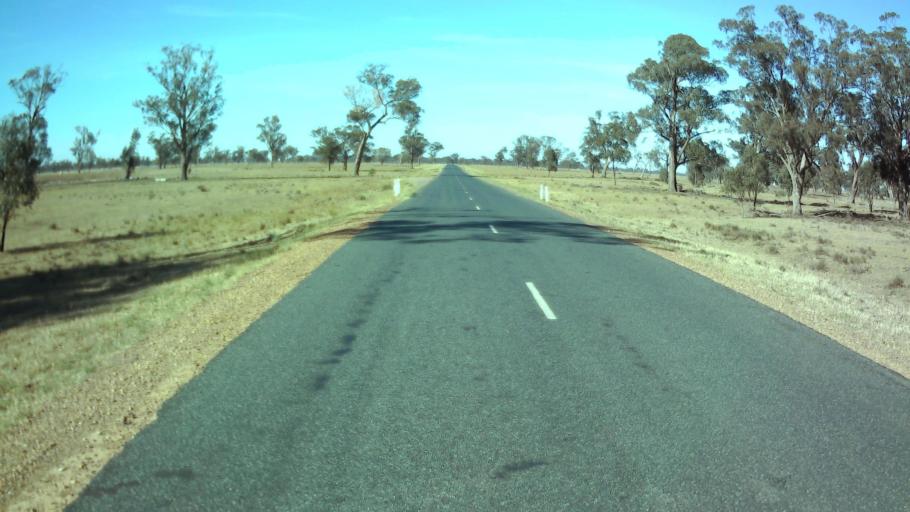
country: AU
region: New South Wales
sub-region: Weddin
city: Grenfell
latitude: -34.0437
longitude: 147.9272
